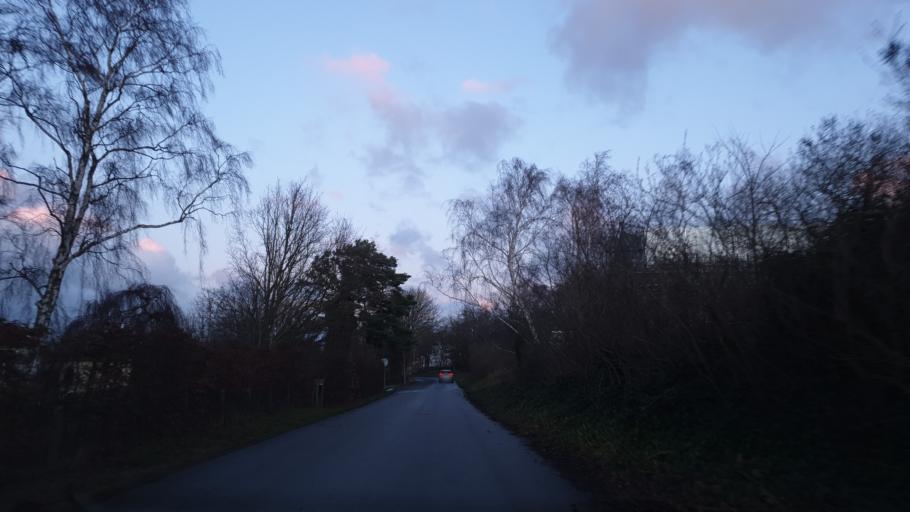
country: SE
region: Skane
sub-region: Vellinge Kommun
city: Skanor med Falsterbo
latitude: 55.3878
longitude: 12.8278
